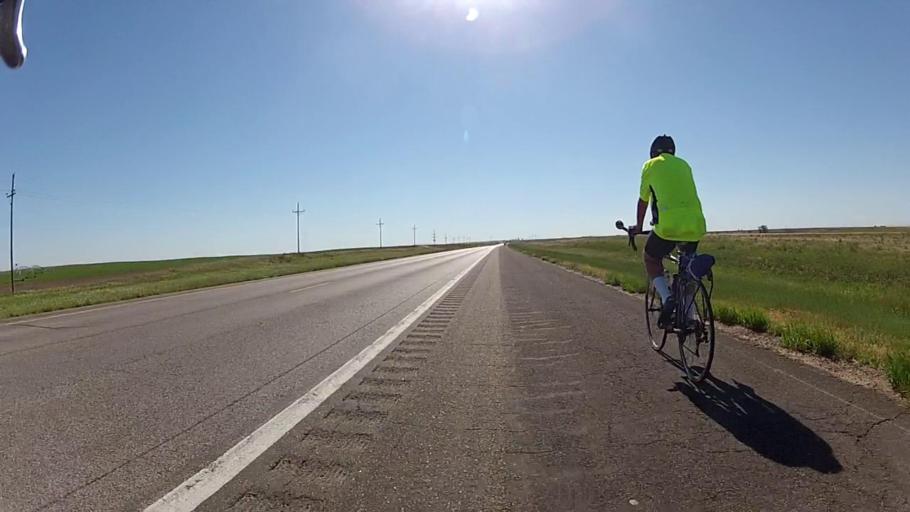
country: US
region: Kansas
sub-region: Kiowa County
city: Greensburg
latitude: 37.5864
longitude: -99.5654
